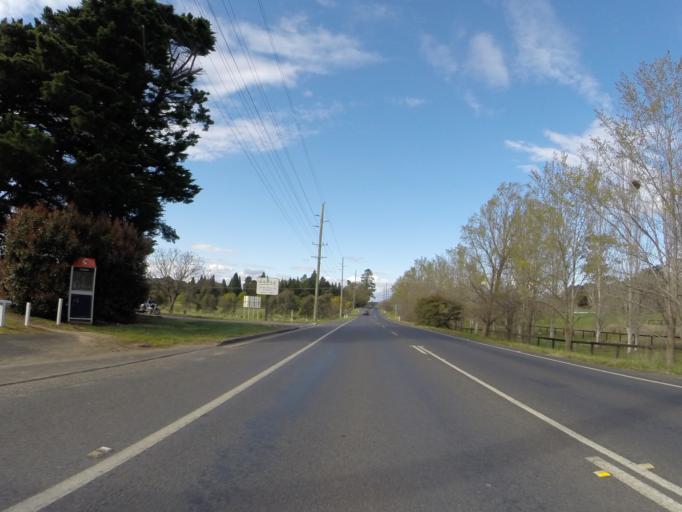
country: AU
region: New South Wales
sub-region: Wingecarribee
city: Moss Vale
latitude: -34.5705
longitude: 150.3180
